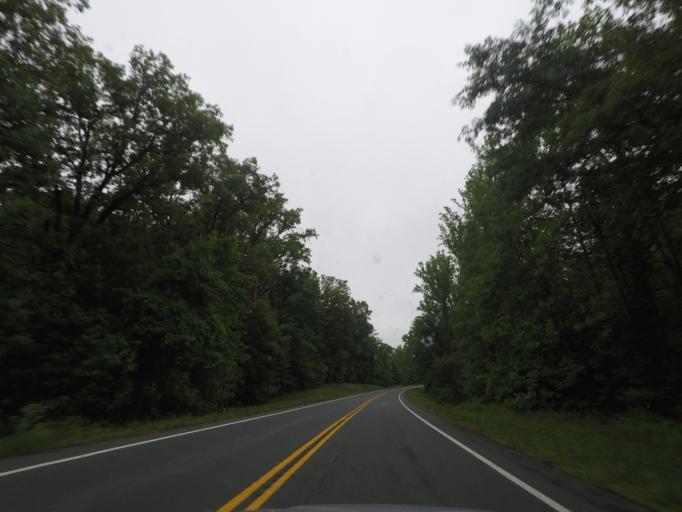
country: US
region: Virginia
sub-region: Fluvanna County
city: Weber City
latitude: 37.7314
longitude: -78.2969
